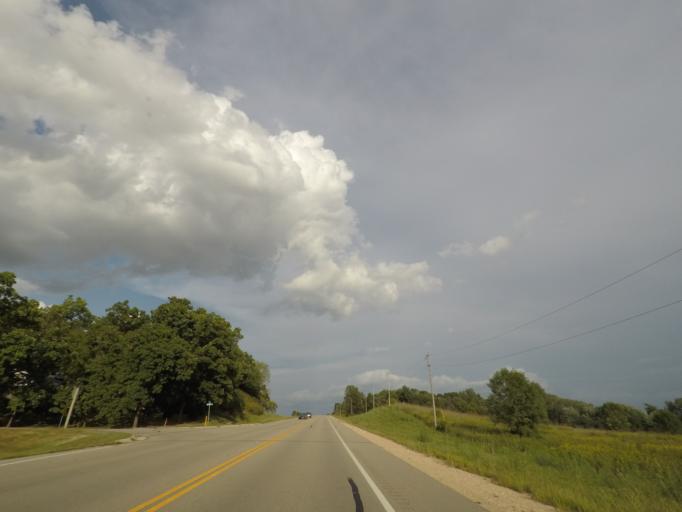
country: US
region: Wisconsin
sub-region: Dane County
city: Waunakee
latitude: 43.1917
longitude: -89.5303
